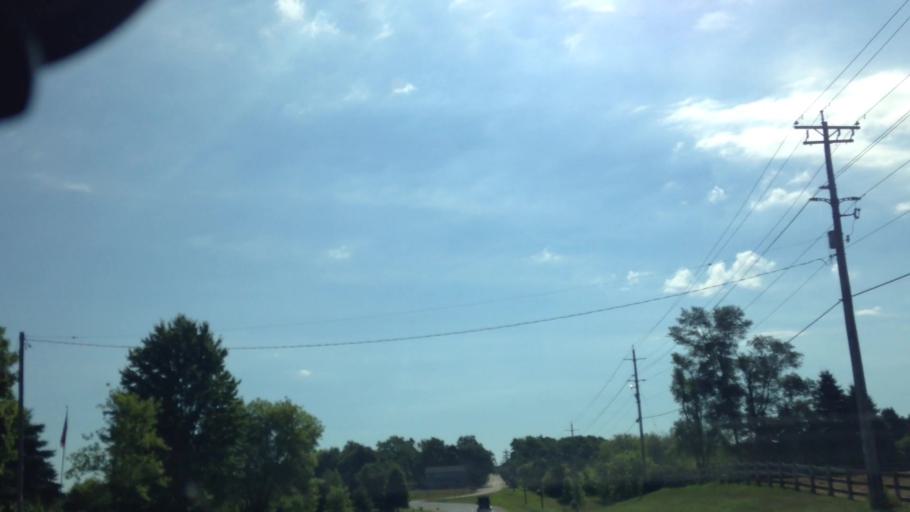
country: US
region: Wisconsin
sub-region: Washington County
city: Slinger
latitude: 43.3534
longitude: -88.2670
